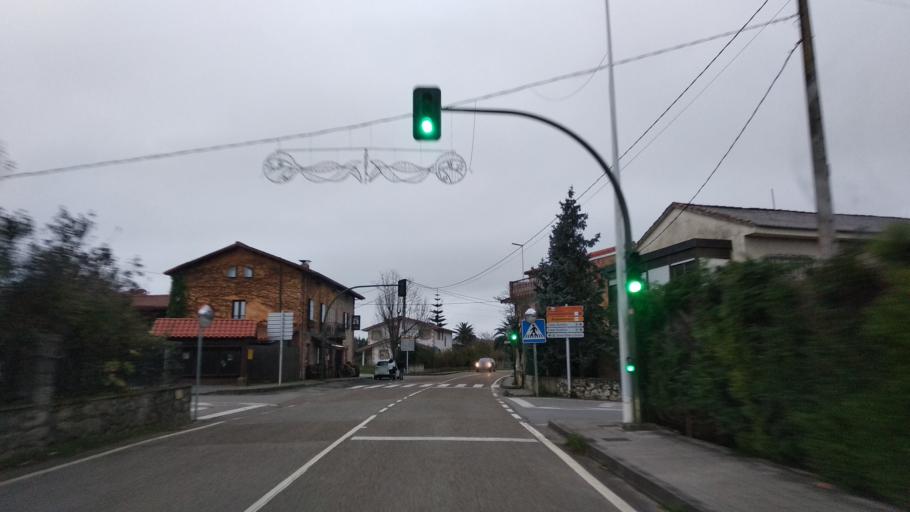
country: ES
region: Cantabria
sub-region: Provincia de Cantabria
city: Santander
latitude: 43.4515
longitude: -3.7369
